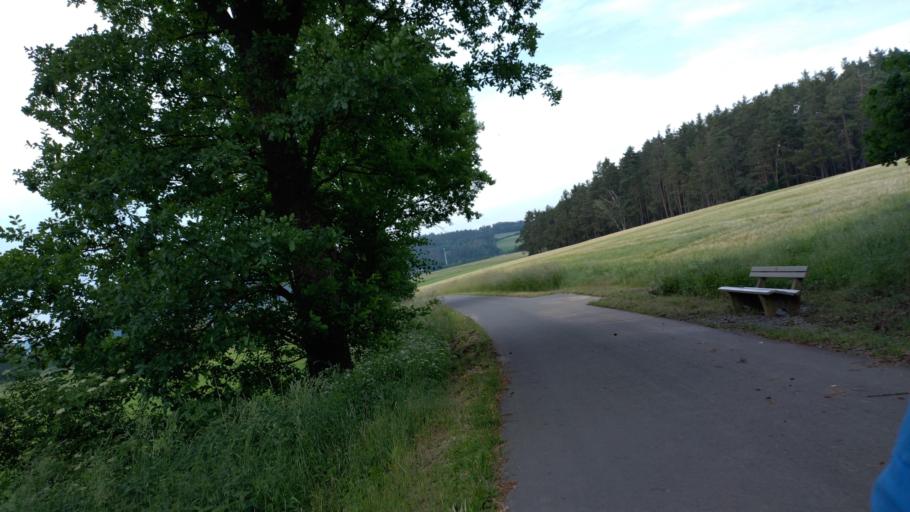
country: DE
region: Bavaria
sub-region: Upper Franconia
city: Harsdorf
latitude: 50.0191
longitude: 11.5764
